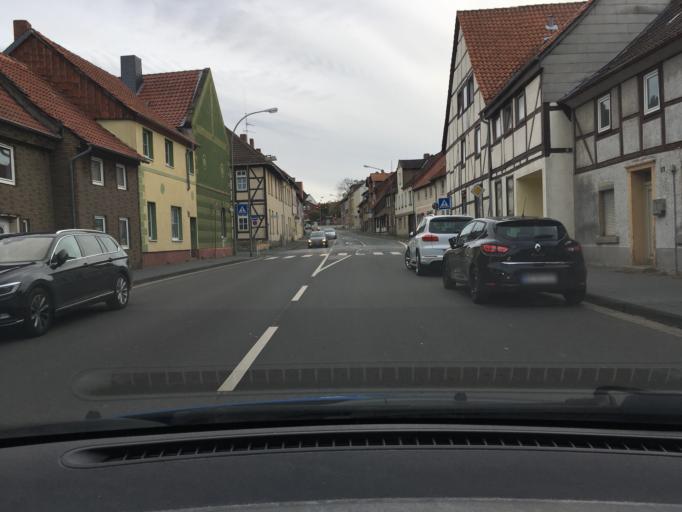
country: DE
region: Lower Saxony
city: Helmstedt
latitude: 52.2291
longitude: 11.0043
